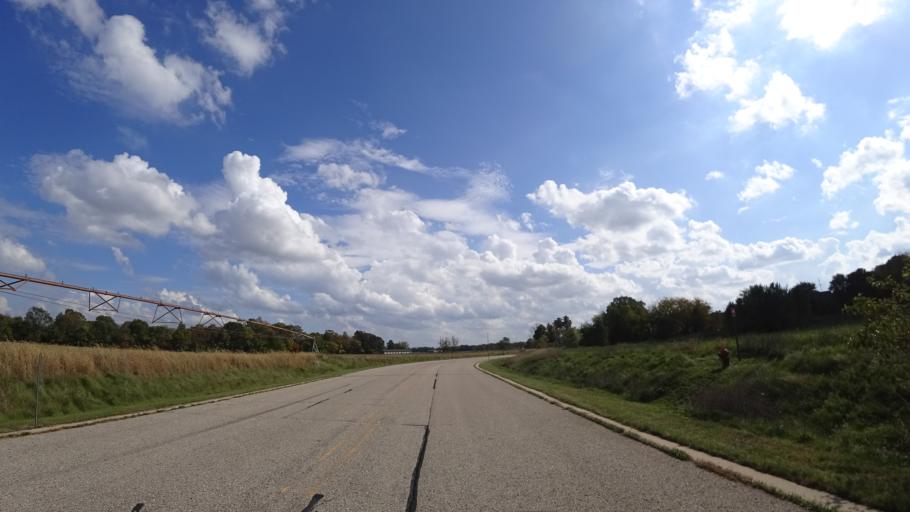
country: US
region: Michigan
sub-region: Saint Joseph County
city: Three Rivers
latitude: 41.9574
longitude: -85.6110
